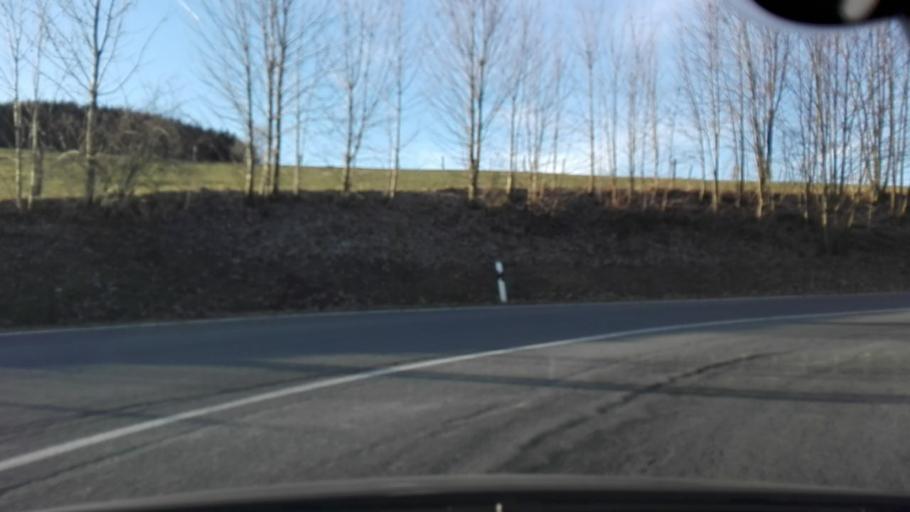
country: DE
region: North Rhine-Westphalia
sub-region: Regierungsbezirk Arnsberg
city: Lennestadt
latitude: 51.1866
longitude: 8.0993
